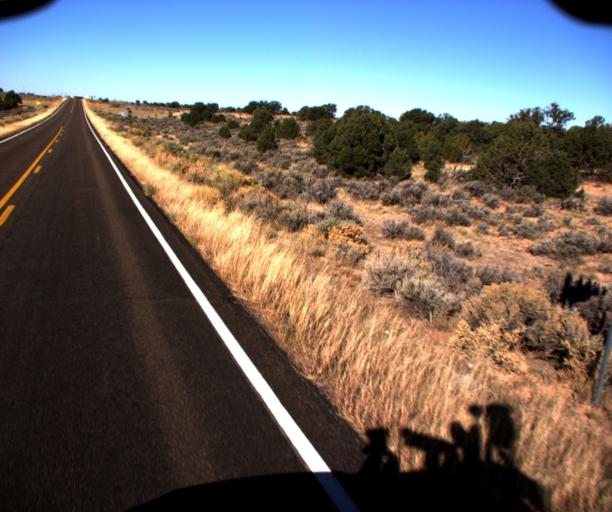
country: US
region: Arizona
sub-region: Navajo County
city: First Mesa
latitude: 35.7332
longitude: -110.1018
